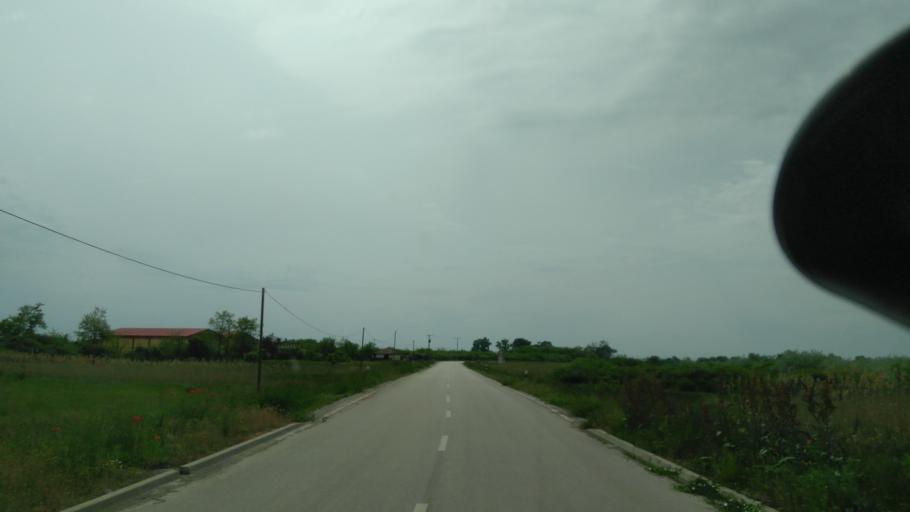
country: HU
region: Bekes
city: Mehkerek
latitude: 46.8673
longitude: 21.5115
